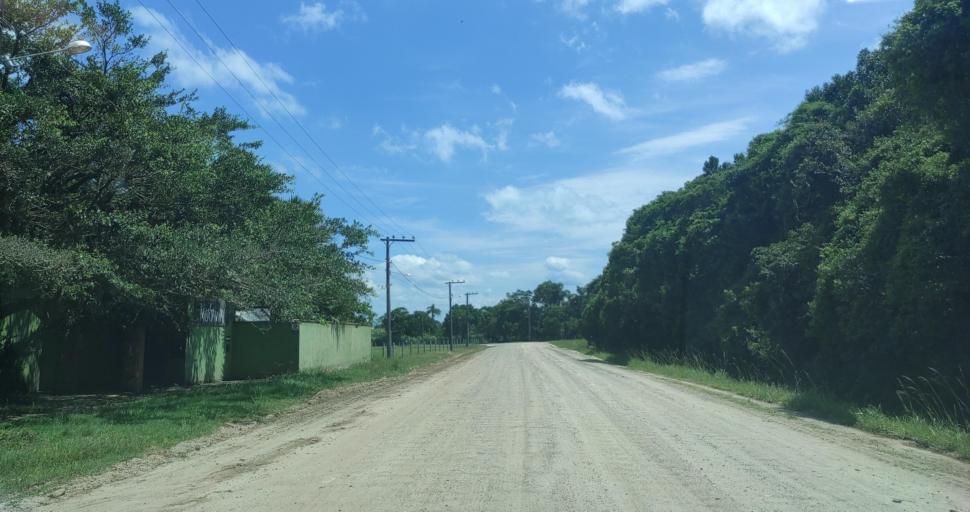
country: BR
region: Santa Catarina
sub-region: Porto Belo
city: Porto Belo
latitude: -27.1812
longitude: -48.5102
